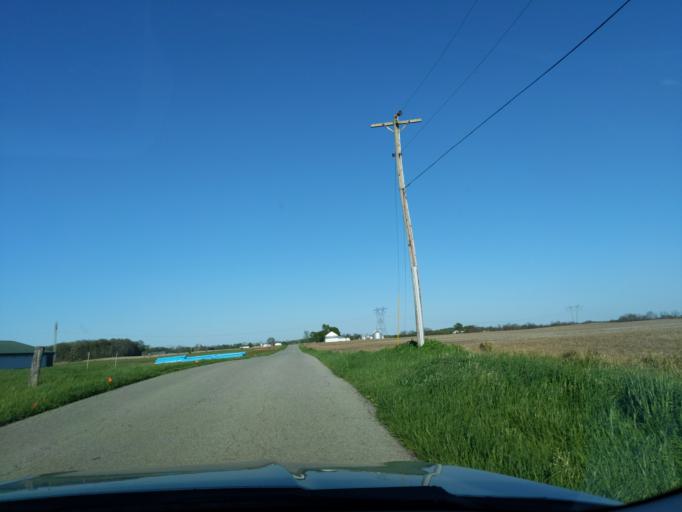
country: US
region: Indiana
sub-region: Decatur County
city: Westport
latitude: 39.1980
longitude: -85.5736
